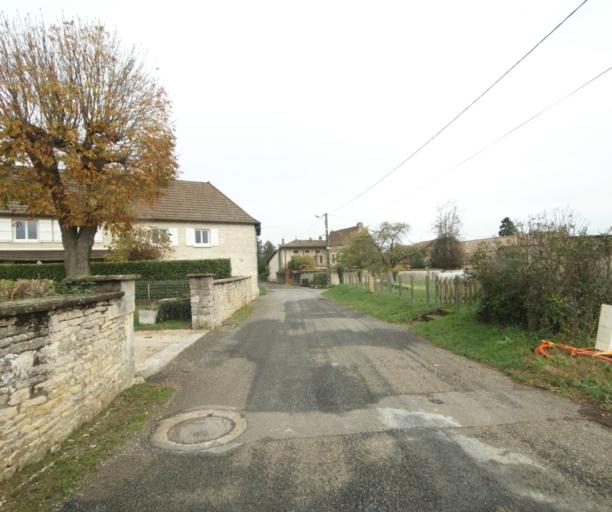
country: FR
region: Rhone-Alpes
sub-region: Departement de l'Ain
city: Pont-de-Vaux
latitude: 46.4645
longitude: 4.8831
